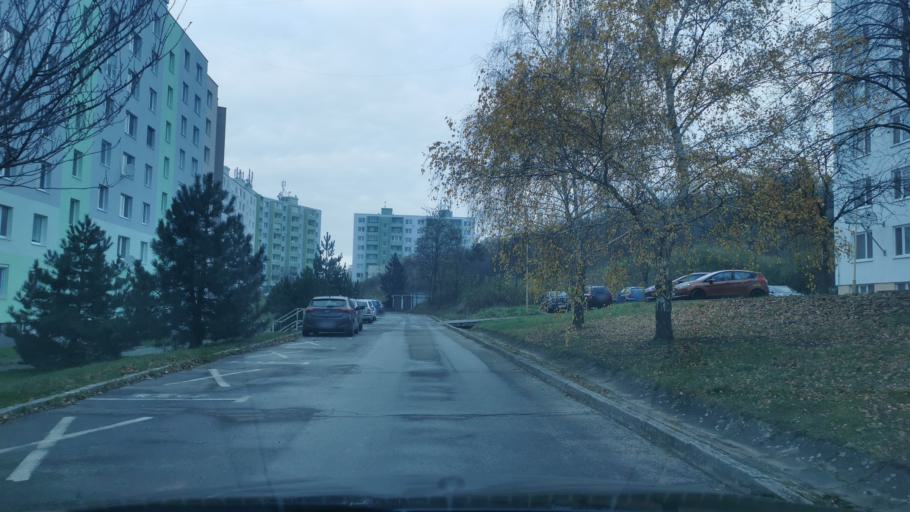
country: SK
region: Trnavsky
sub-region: Okres Skalica
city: Holic
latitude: 48.8043
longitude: 17.1650
